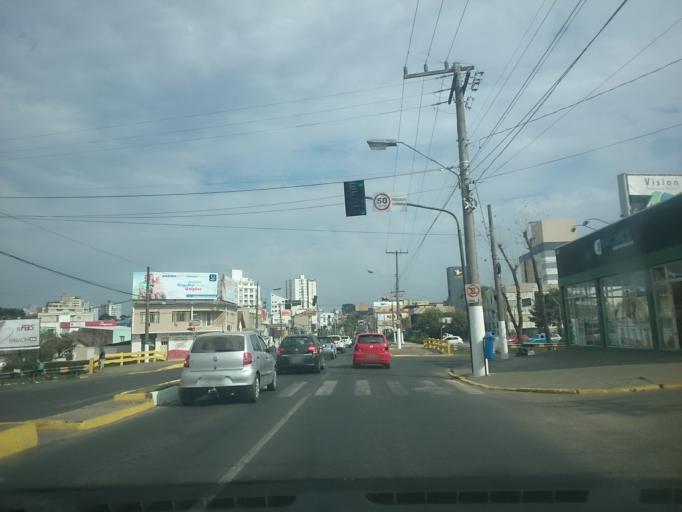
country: BR
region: Santa Catarina
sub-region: Lages
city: Lages
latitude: -27.8109
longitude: -50.3172
